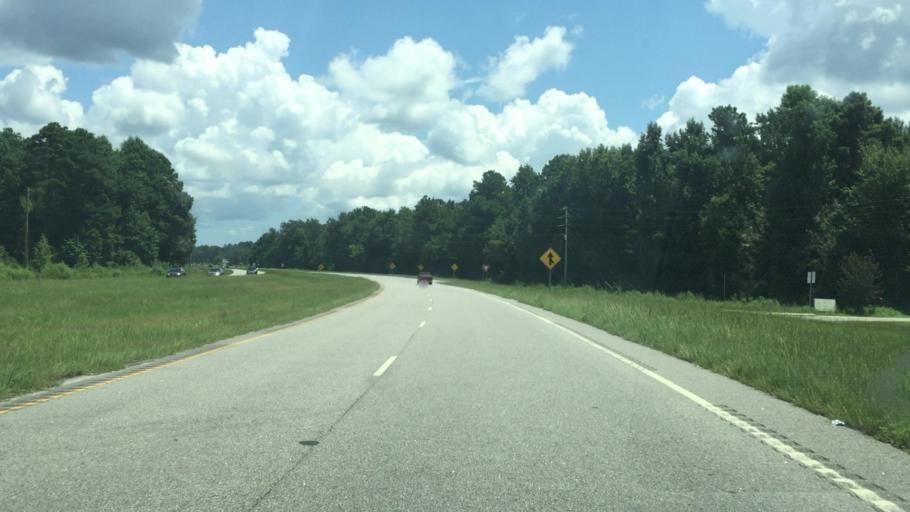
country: US
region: South Carolina
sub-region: Horry County
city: Loris
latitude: 34.0179
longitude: -78.7932
